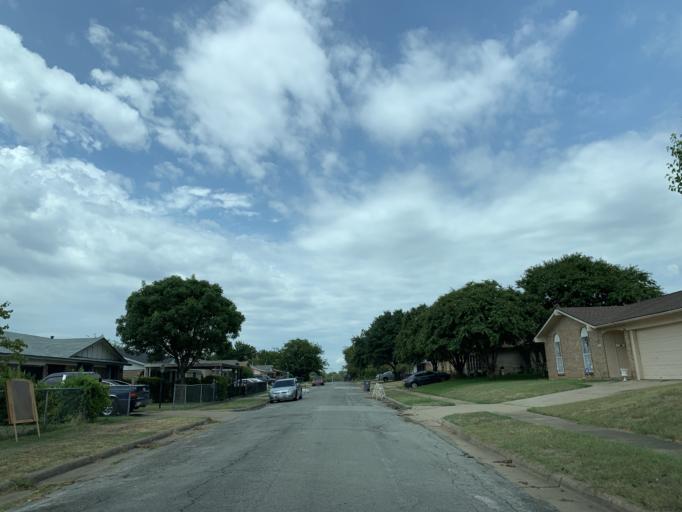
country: US
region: Texas
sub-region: Dallas County
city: DeSoto
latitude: 32.6590
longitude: -96.8131
